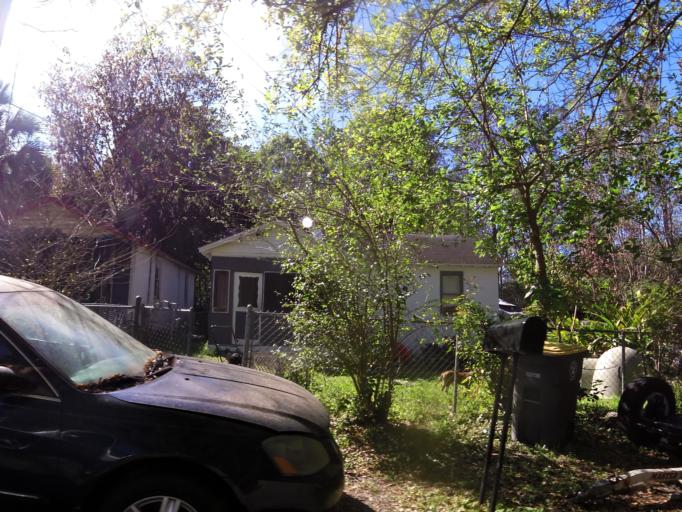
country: US
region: Florida
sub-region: Duval County
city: Jacksonville
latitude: 30.3635
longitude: -81.6470
